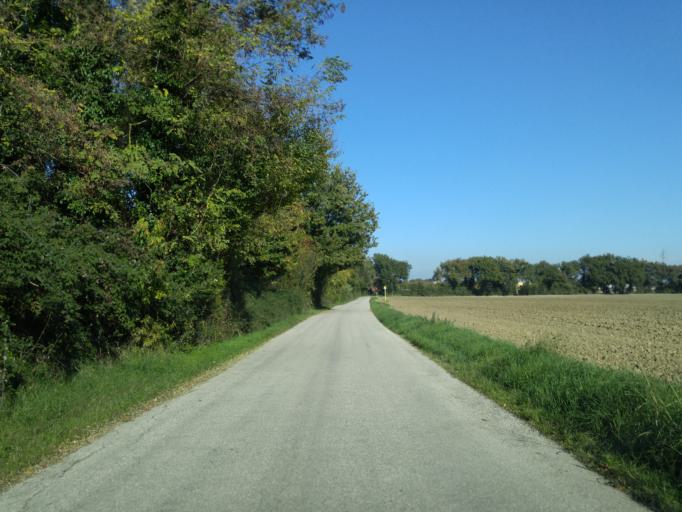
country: IT
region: The Marches
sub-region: Provincia di Pesaro e Urbino
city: Tavernelle
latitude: 43.7210
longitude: 12.8884
